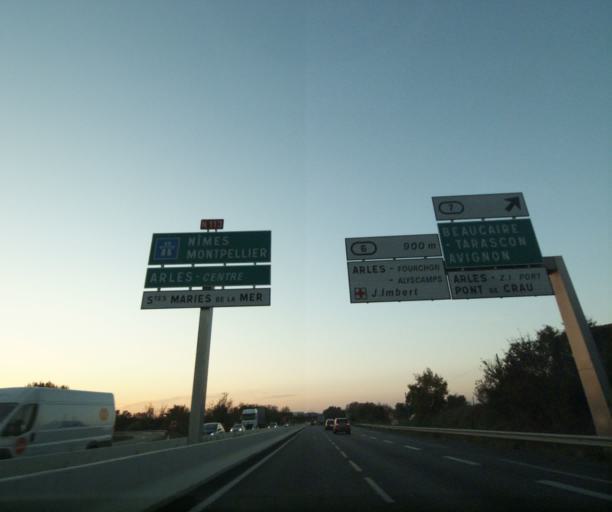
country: FR
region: Provence-Alpes-Cote d'Azur
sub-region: Departement des Bouches-du-Rhone
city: Arles
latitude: 43.6601
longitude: 4.6425
